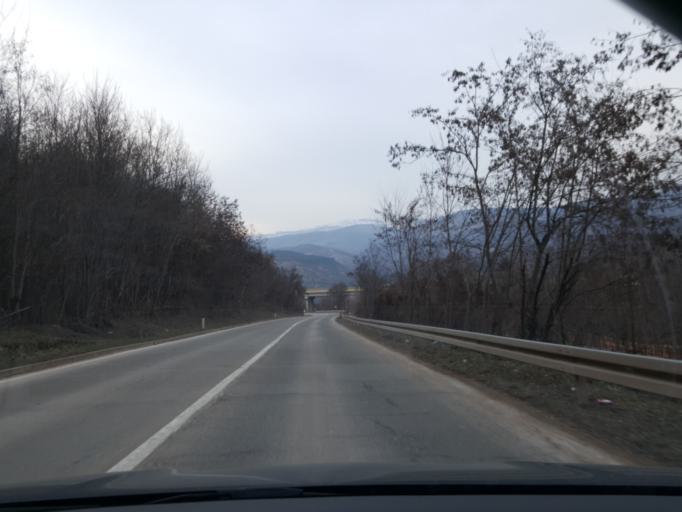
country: RS
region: Central Serbia
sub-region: Pirotski Okrug
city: Bela Palanka
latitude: 43.2557
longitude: 22.2615
